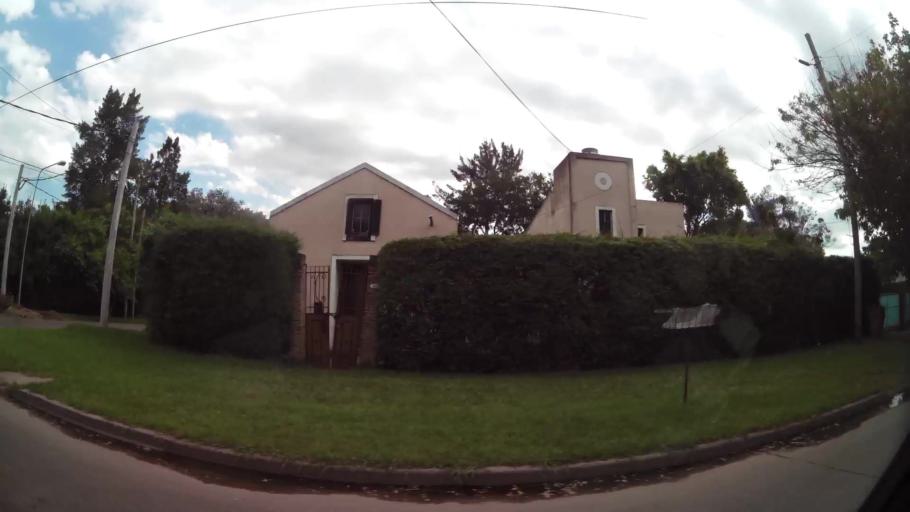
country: AR
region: Buenos Aires
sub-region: Partido de Tigre
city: Tigre
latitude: -34.4763
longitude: -58.6428
